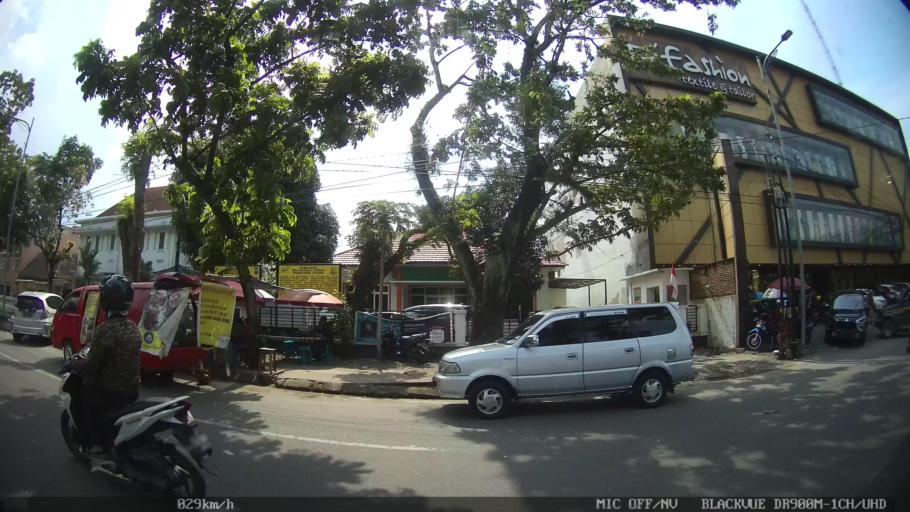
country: ID
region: North Sumatra
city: Medan
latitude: 3.5868
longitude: 98.6611
